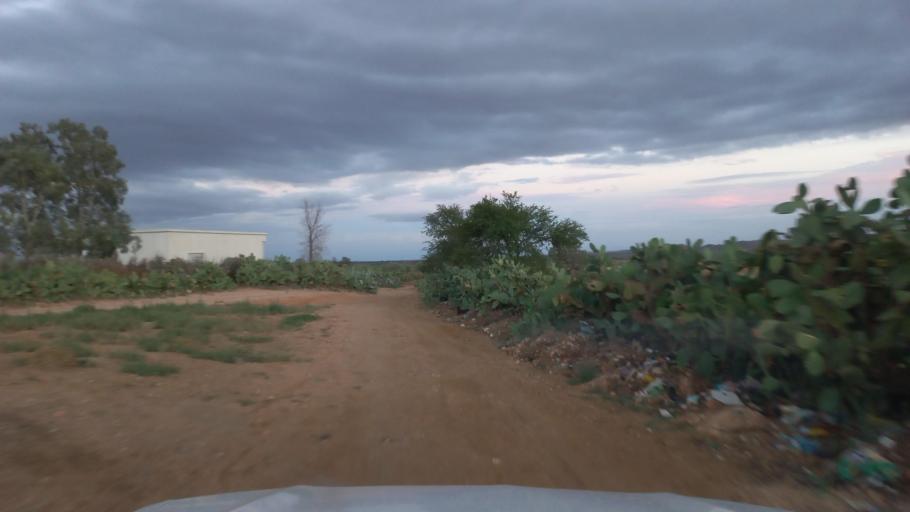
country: TN
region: Al Qasrayn
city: Kasserine
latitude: 35.2566
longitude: 8.9394
